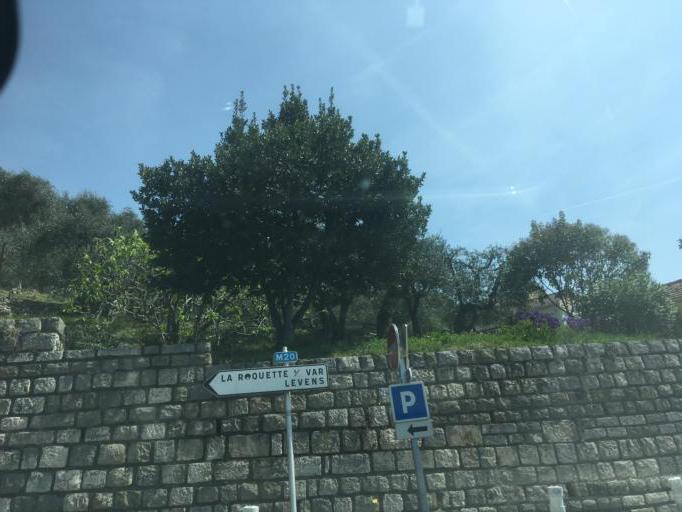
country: FR
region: Provence-Alpes-Cote d'Azur
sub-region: Departement des Alpes-Maritimes
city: Saint-Martin-du-Var
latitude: 43.8247
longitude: 7.1899
